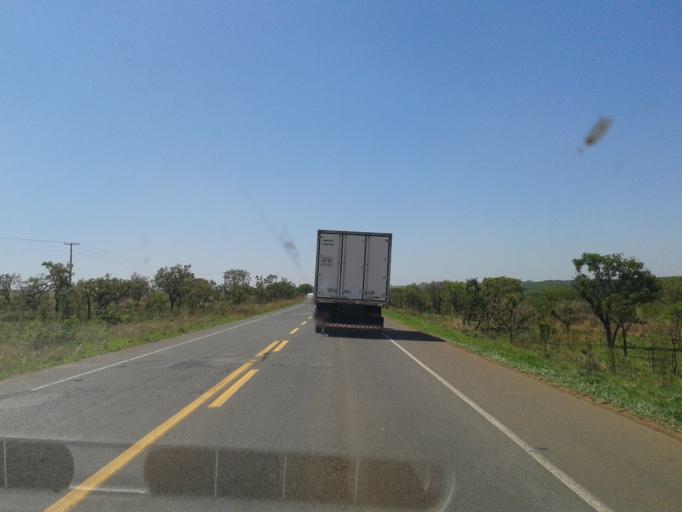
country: BR
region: Minas Gerais
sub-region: Patrocinio
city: Patrocinio
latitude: -19.2815
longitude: -47.4231
